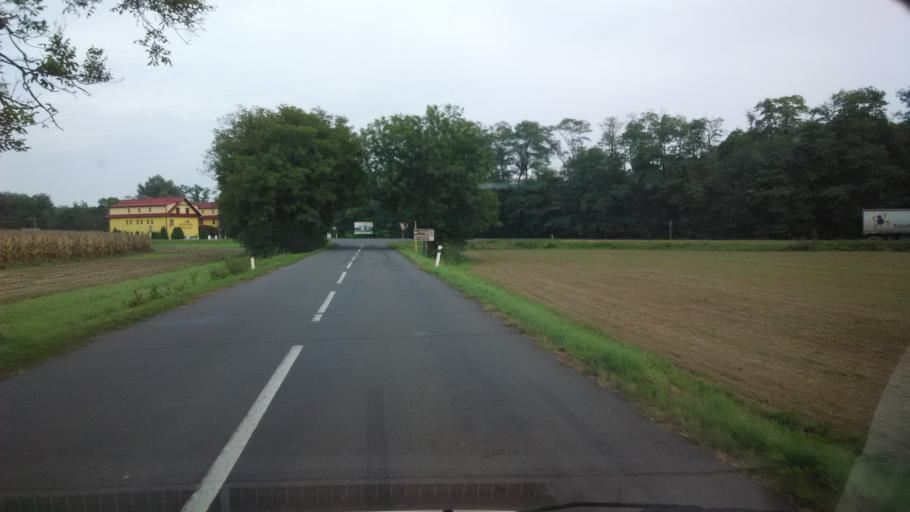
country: SK
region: Banskobystricky
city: Dudince
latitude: 48.1680
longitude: 18.8714
